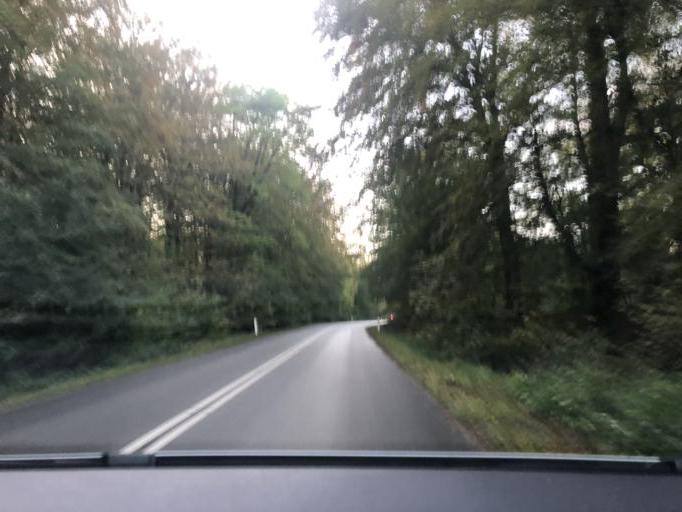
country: DK
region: Capital Region
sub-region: Frederikssund Kommune
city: Slangerup
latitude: 55.8153
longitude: 12.2044
